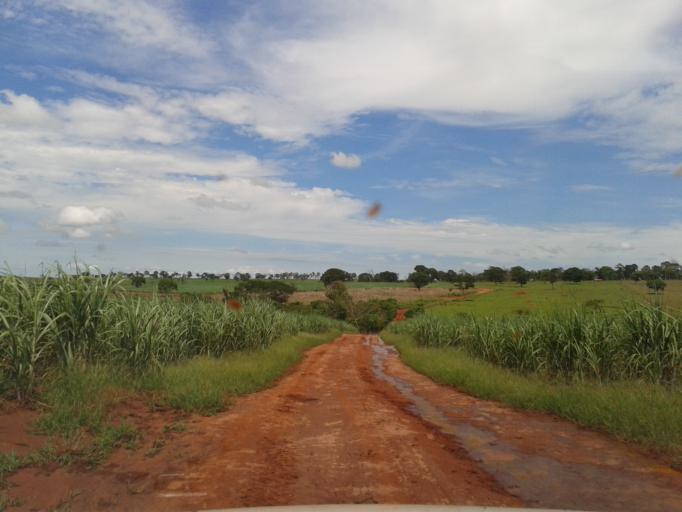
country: BR
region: Minas Gerais
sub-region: Santa Vitoria
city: Santa Vitoria
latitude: -19.2093
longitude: -50.6352
